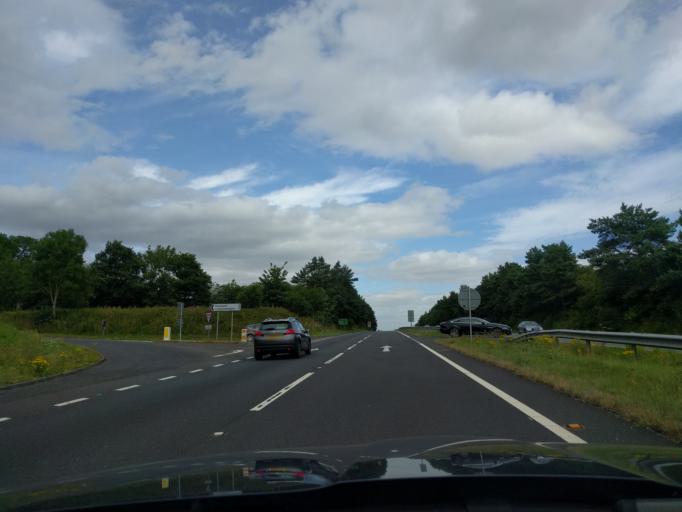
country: GB
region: England
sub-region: Northumberland
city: Felton
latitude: 55.3181
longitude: -1.7250
